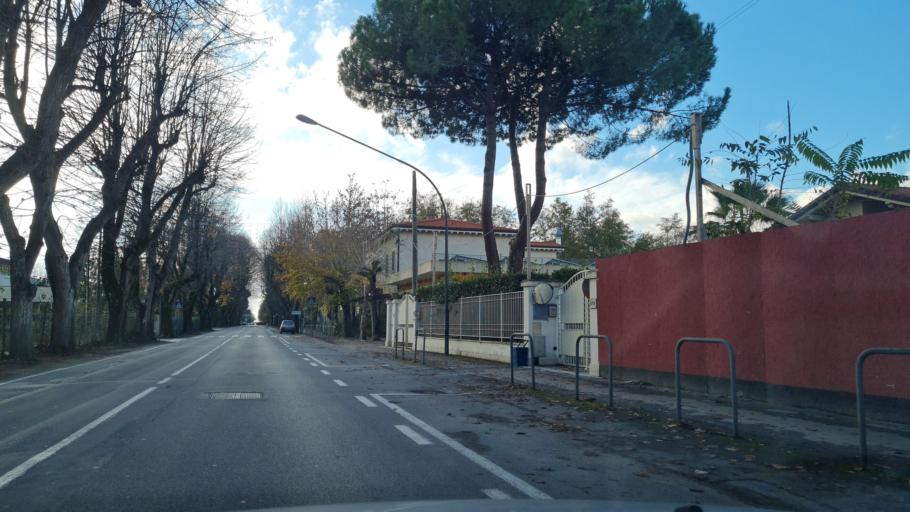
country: IT
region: Tuscany
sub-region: Provincia di Lucca
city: Pietrasanta
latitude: 43.9433
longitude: 10.2021
